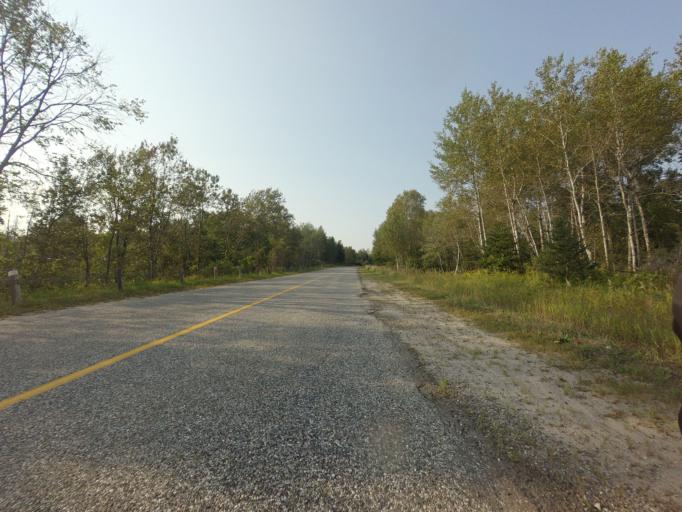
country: CA
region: Ontario
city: Perth
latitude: 44.9318
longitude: -76.6871
